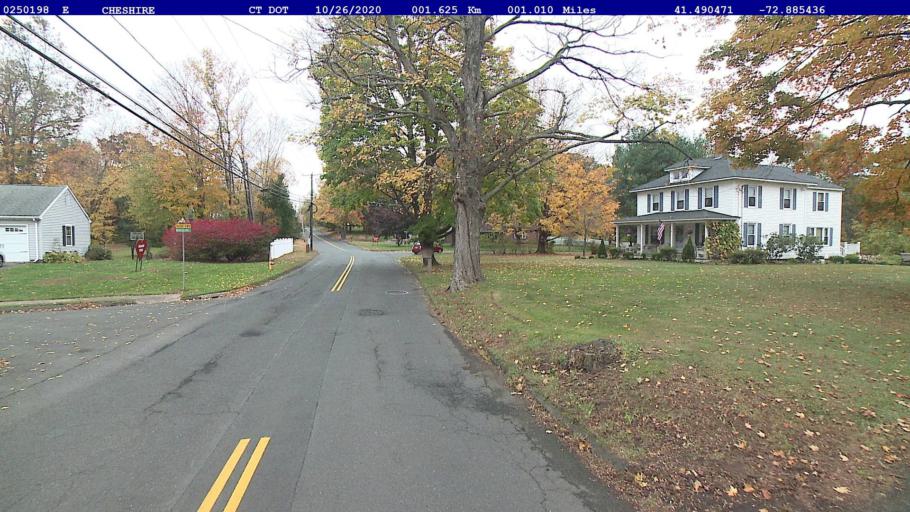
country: US
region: Connecticut
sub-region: New Haven County
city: Cheshire
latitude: 41.4905
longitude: -72.8854
